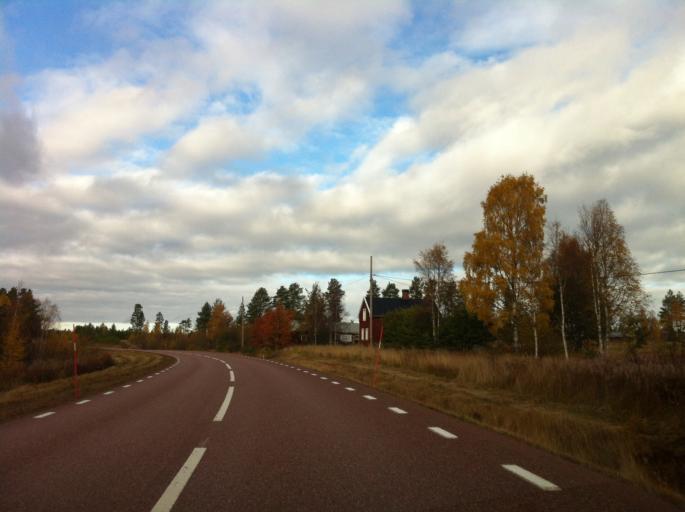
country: SE
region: Dalarna
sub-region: Alvdalens Kommun
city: AElvdalen
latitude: 61.5306
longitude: 13.3574
